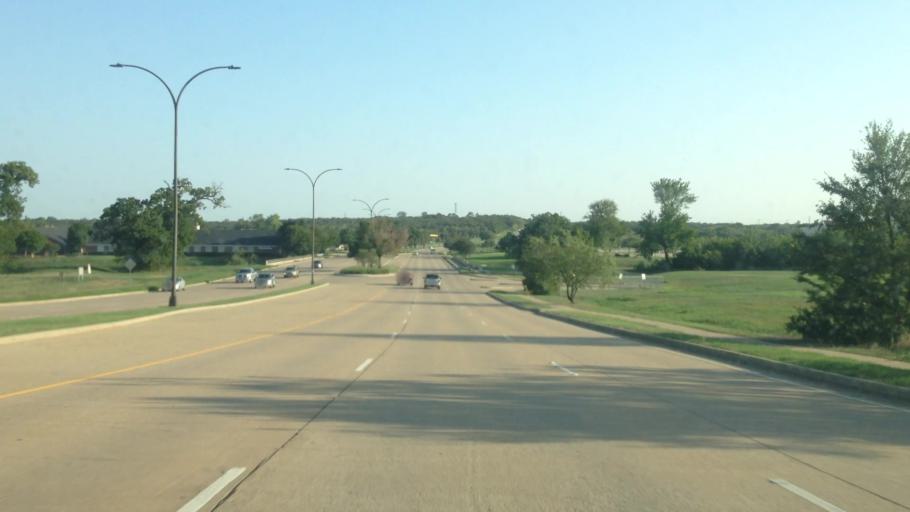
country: US
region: Texas
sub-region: Tarrant County
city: Pantego
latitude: 32.7294
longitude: -97.1814
